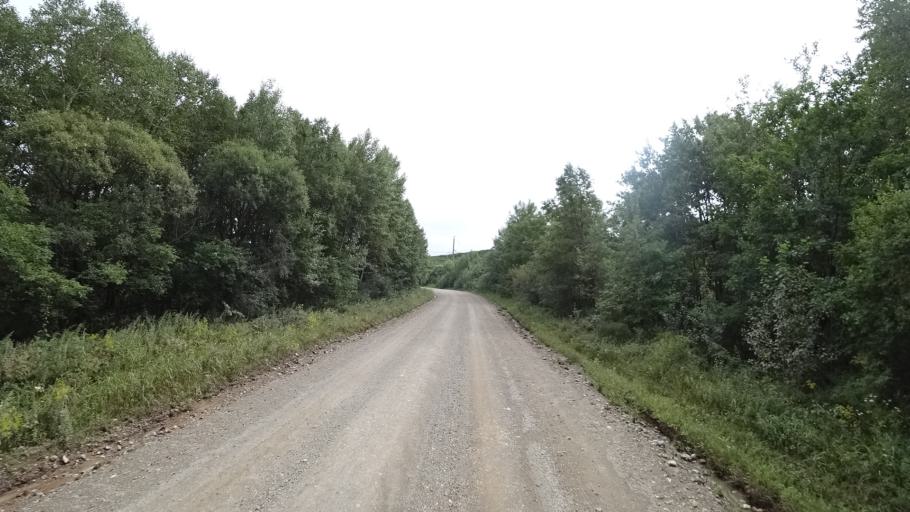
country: RU
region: Primorskiy
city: Lyalichi
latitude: 44.0897
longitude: 132.4346
